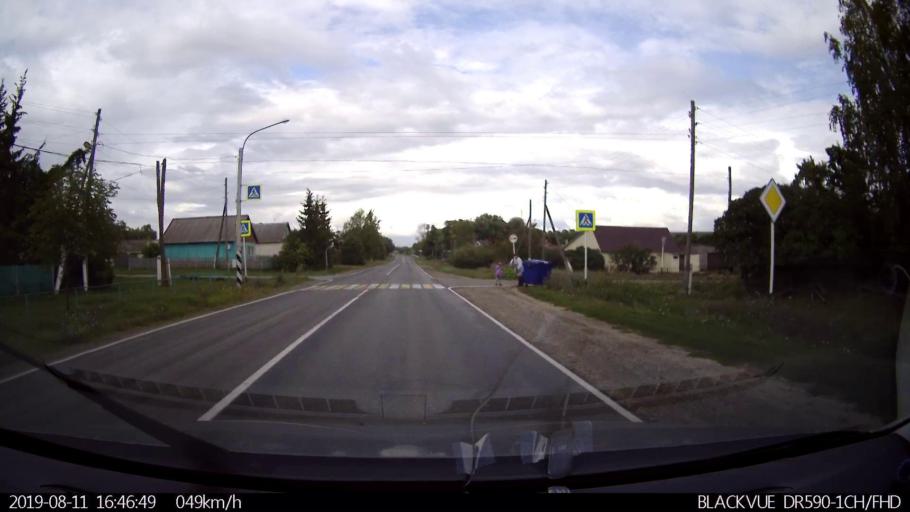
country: RU
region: Ulyanovsk
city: Mayna
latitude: 54.1998
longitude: 47.6919
